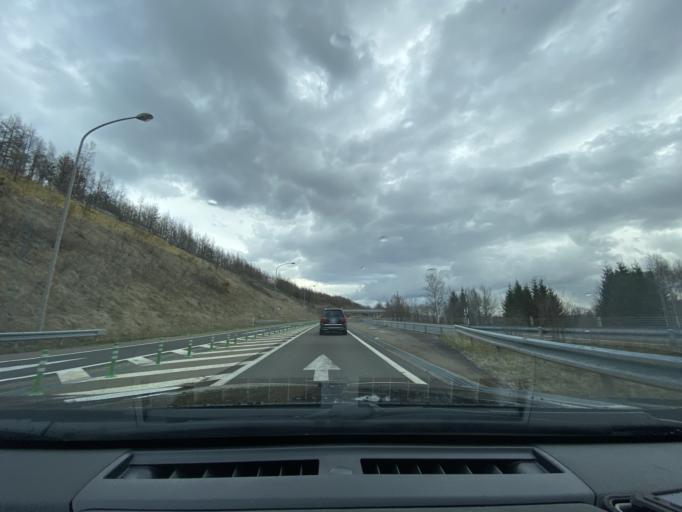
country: JP
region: Hokkaido
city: Otofuke
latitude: 42.9820
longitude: 143.0240
